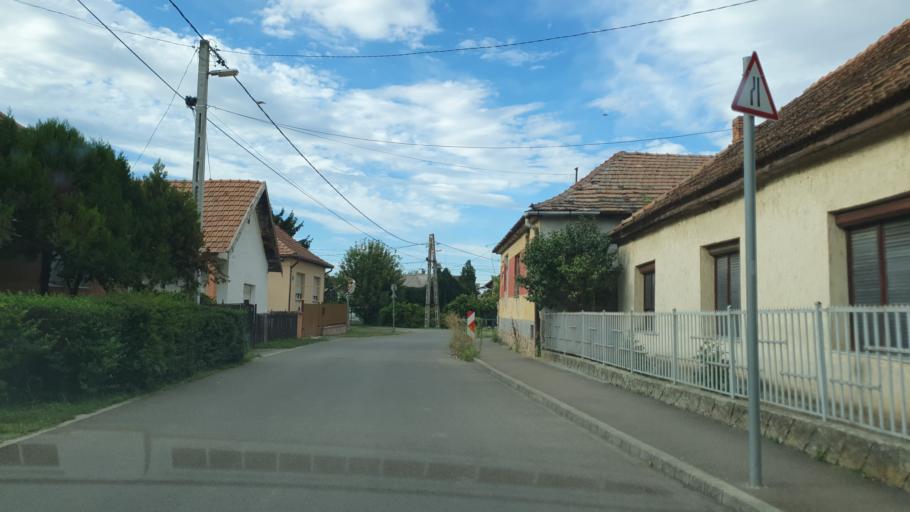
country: HU
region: Heves
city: Lorinci
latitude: 47.7452
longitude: 19.6748
